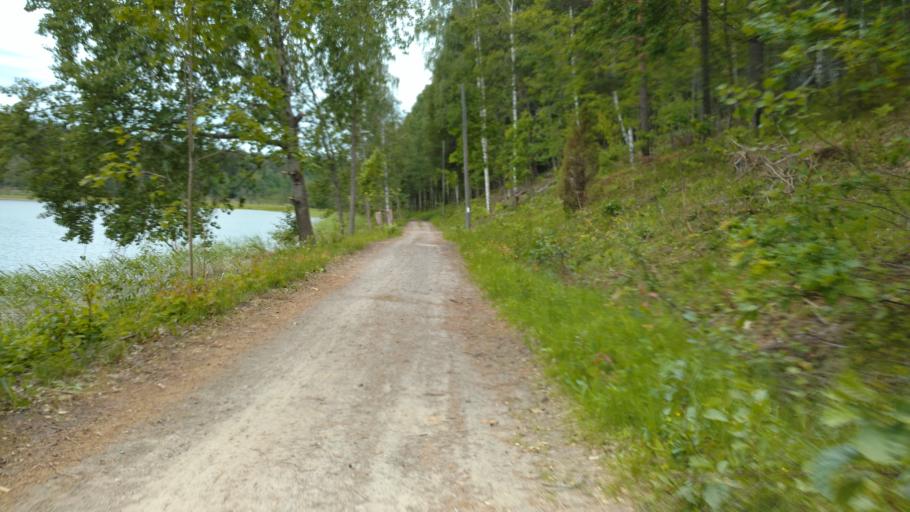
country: FI
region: Uusimaa
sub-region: Raaseporin
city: Pohja
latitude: 60.1174
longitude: 23.5418
